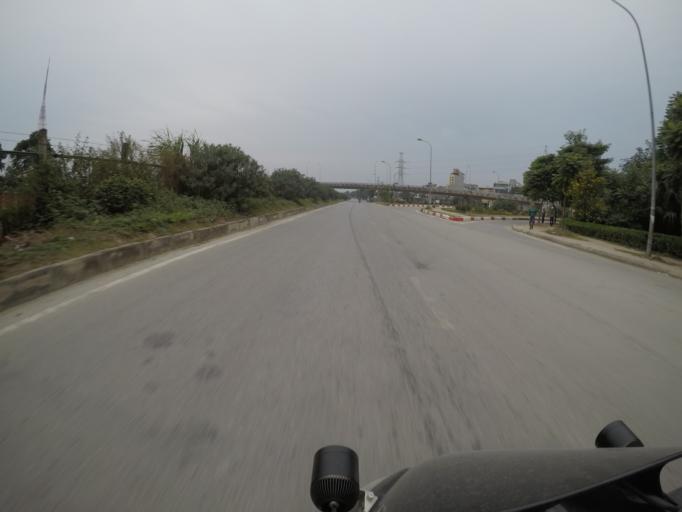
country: VN
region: Ha Noi
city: Cau Dien
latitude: 21.0061
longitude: 105.7680
